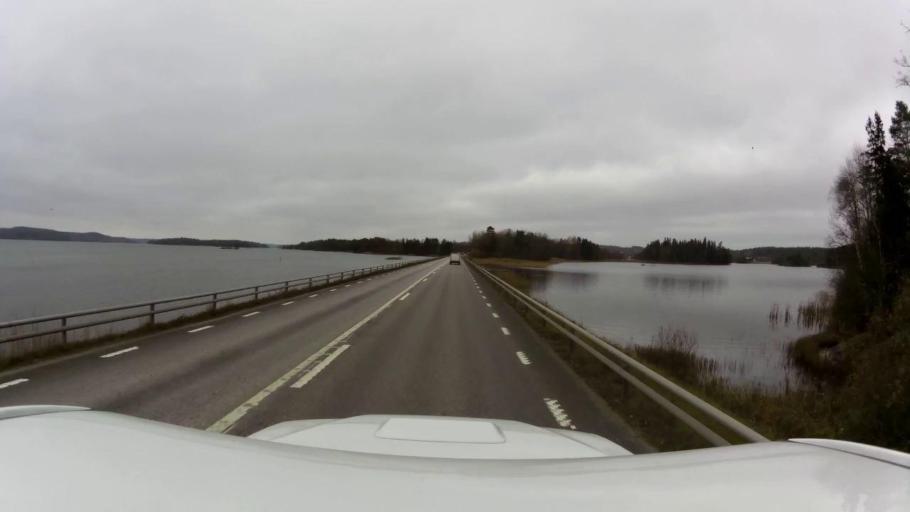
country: SE
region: OEstergoetland
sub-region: Kinda Kommun
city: Rimforsa
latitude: 58.1515
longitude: 15.6801
